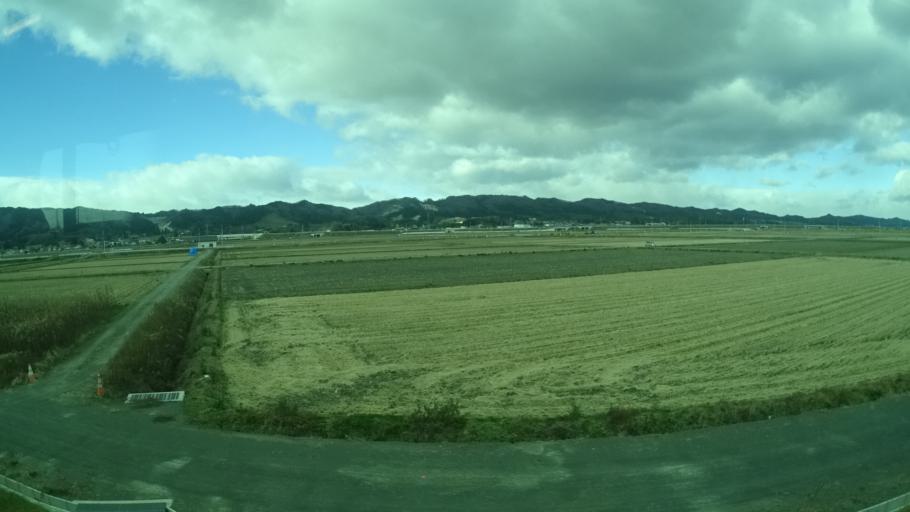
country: JP
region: Miyagi
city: Watari
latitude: 37.9799
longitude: 140.8875
